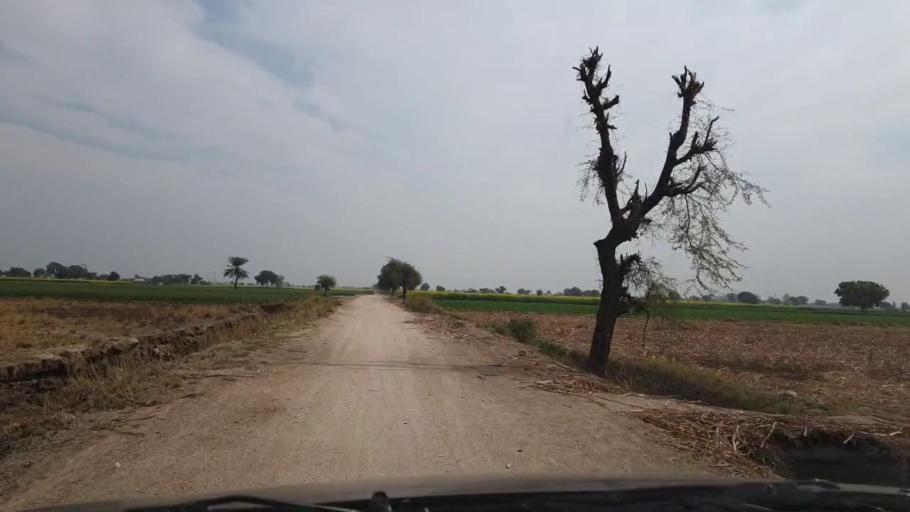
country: PK
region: Sindh
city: Sinjhoro
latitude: 26.0650
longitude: 68.8486
